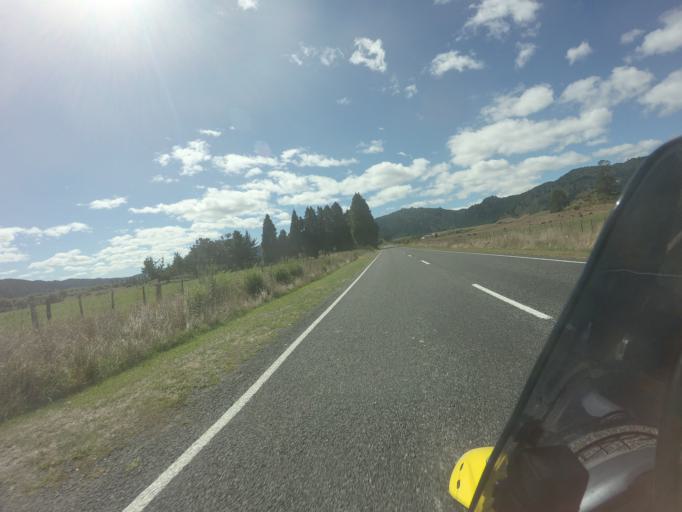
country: NZ
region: Bay of Plenty
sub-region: Kawerau District
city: Kawerau
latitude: -38.2371
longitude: 176.8329
